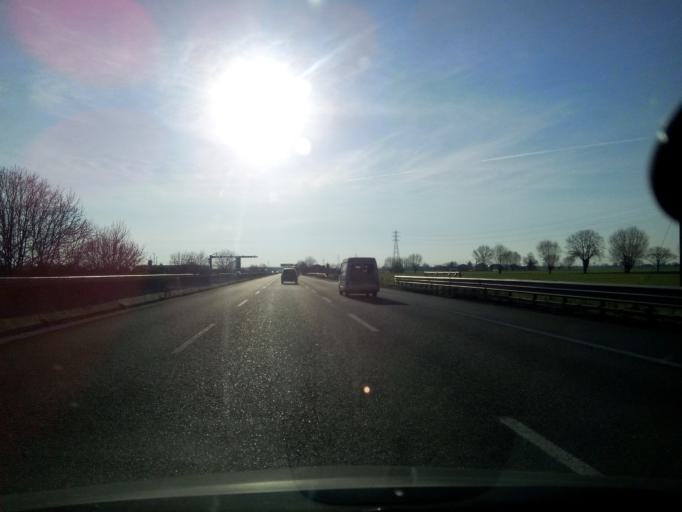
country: IT
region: Emilia-Romagna
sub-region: Provincia di Parma
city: Fontanellato
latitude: 44.8719
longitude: 10.1976
